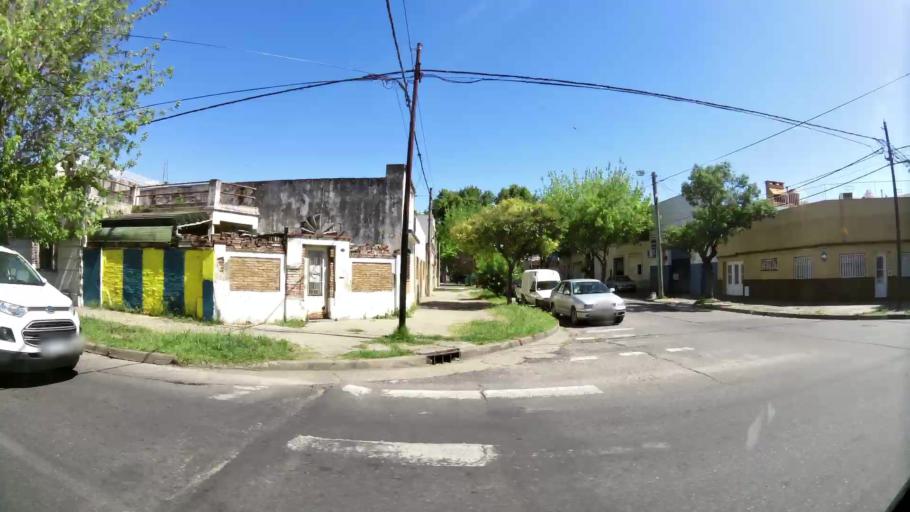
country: AR
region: Santa Fe
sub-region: Departamento de Rosario
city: Rosario
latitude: -32.9361
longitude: -60.6884
